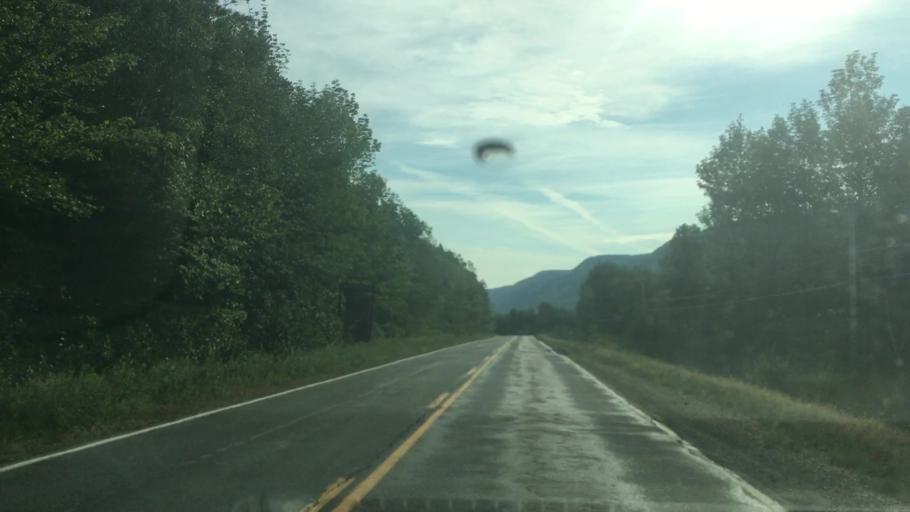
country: CA
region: Nova Scotia
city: Sydney Mines
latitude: 46.8609
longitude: -60.5675
